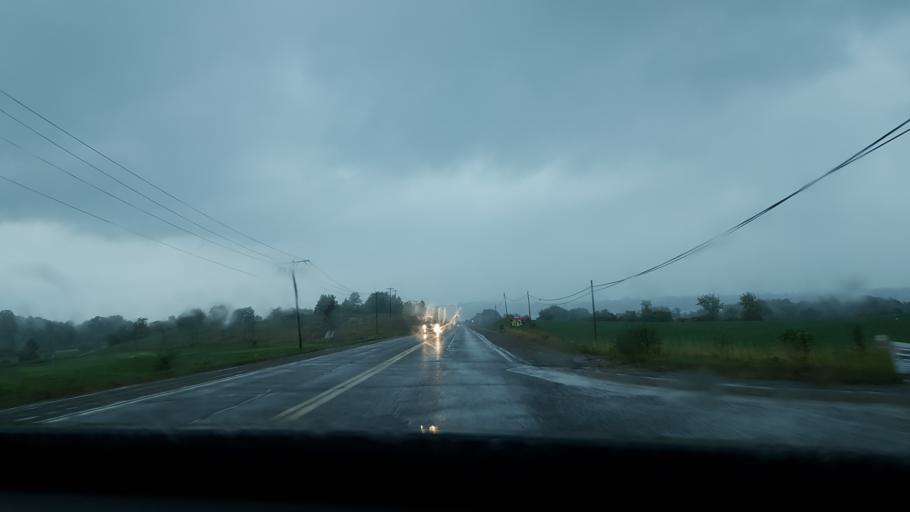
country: CA
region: Ontario
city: Peterborough
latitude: 44.3839
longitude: -78.4148
